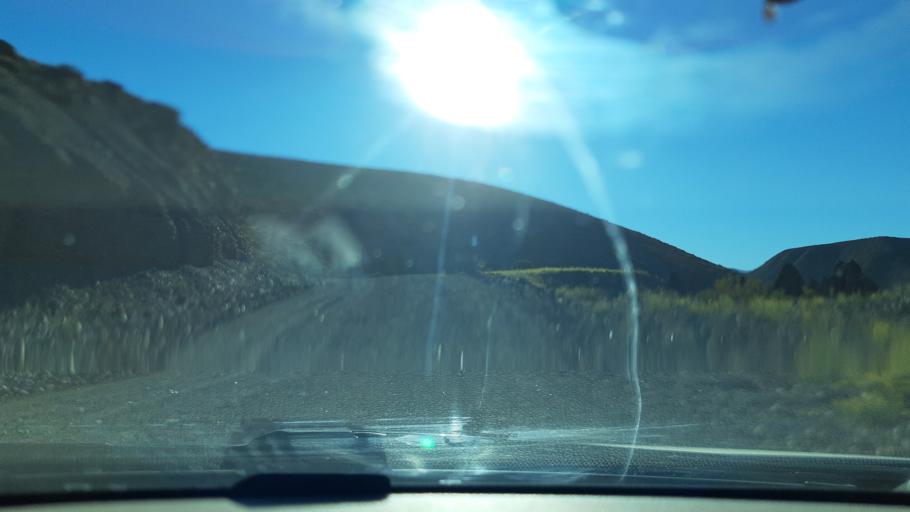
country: AR
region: Neuquen
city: Las Ovejas
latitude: -36.8078
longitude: -70.7189
